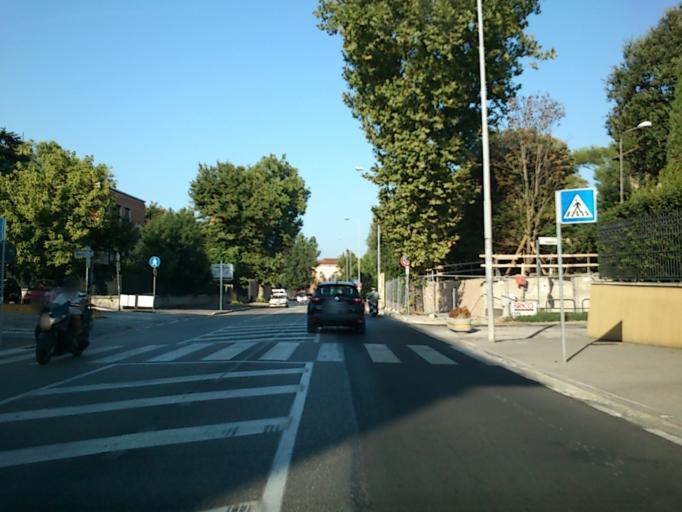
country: IT
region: The Marches
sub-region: Provincia di Pesaro e Urbino
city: Fano
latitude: 43.8414
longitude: 13.0224
